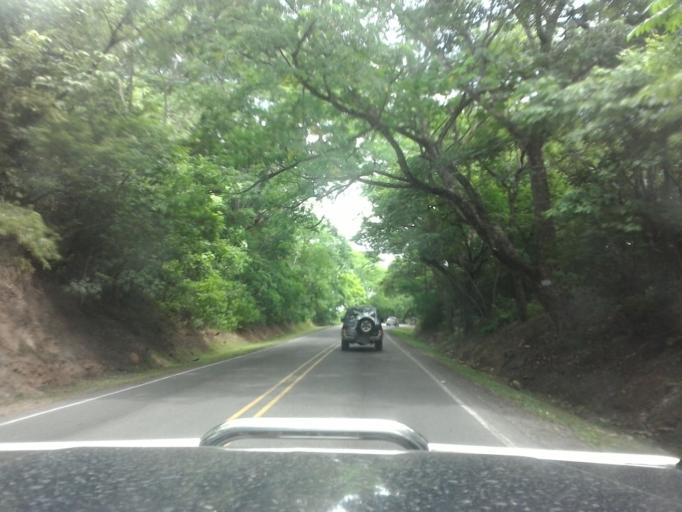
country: CR
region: Puntarenas
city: Miramar
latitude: 10.0832
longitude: -84.7867
